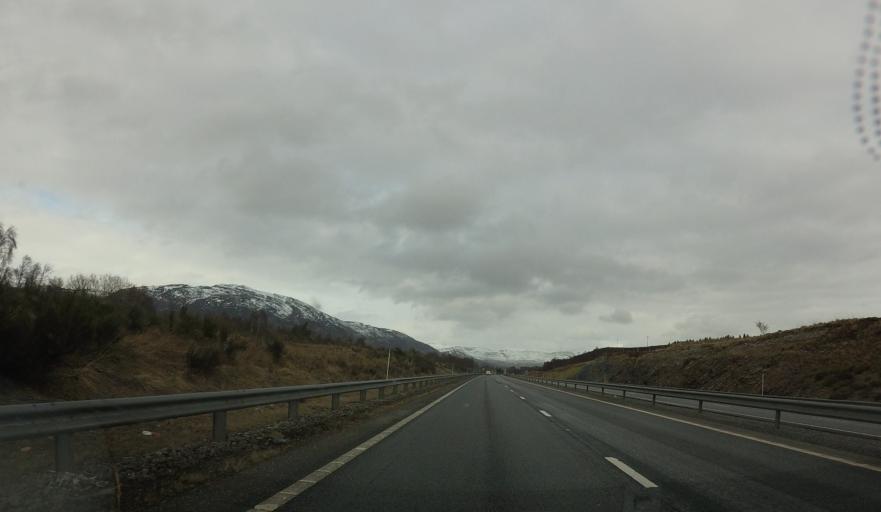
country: GB
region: Scotland
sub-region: Highland
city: Kingussie
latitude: 57.0177
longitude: -4.1611
